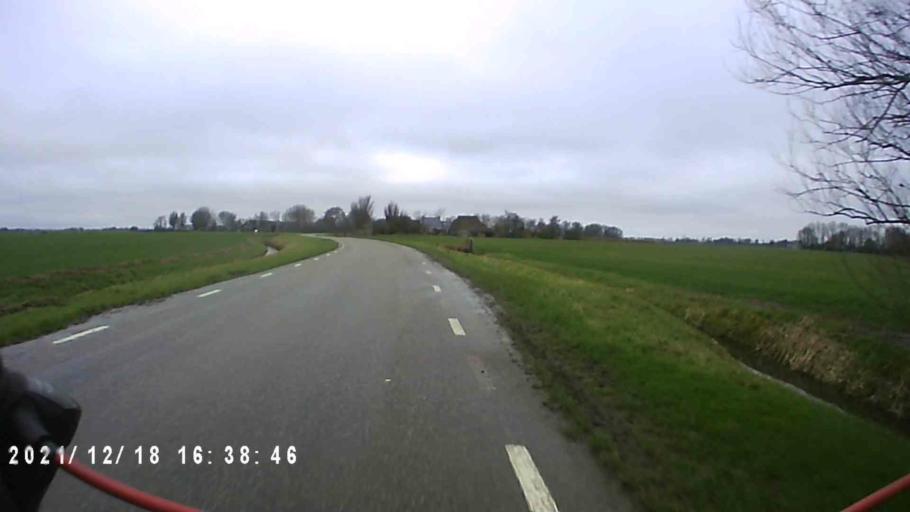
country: NL
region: Friesland
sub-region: Gemeente Dongeradeel
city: Dokkum
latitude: 53.3593
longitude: 6.0099
